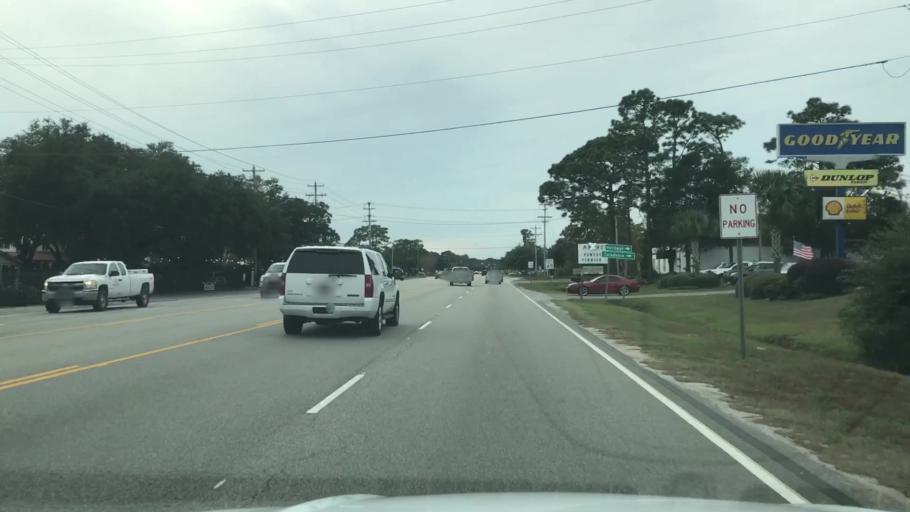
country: US
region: South Carolina
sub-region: Georgetown County
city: Murrells Inlet
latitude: 33.4324
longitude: -79.1409
